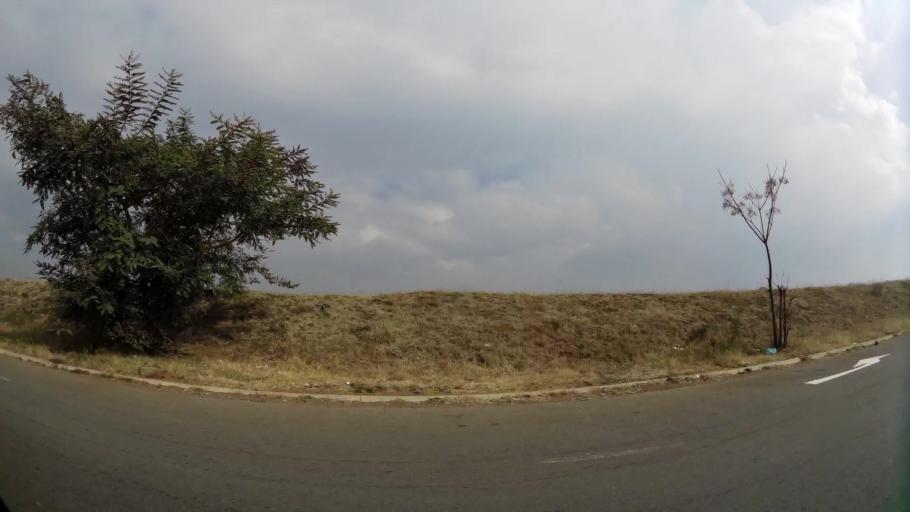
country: ZA
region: Gauteng
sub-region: Sedibeng District Municipality
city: Vanderbijlpark
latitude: -26.6872
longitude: 27.8603
